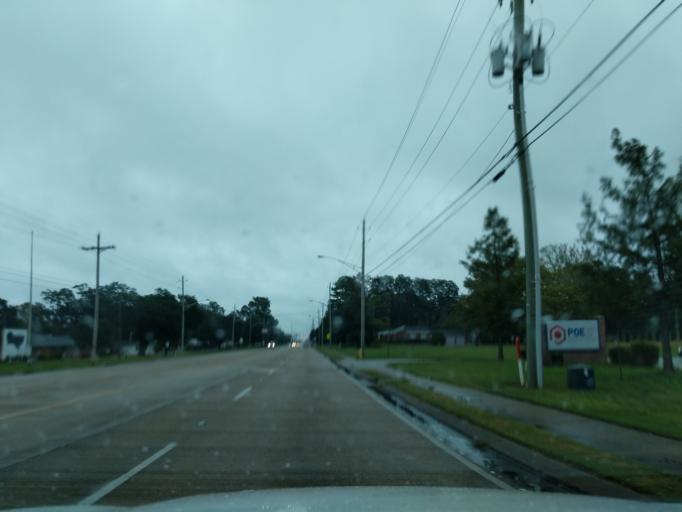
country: US
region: Louisiana
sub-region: Bossier Parish
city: Bossier City
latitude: 32.5190
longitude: -93.7047
